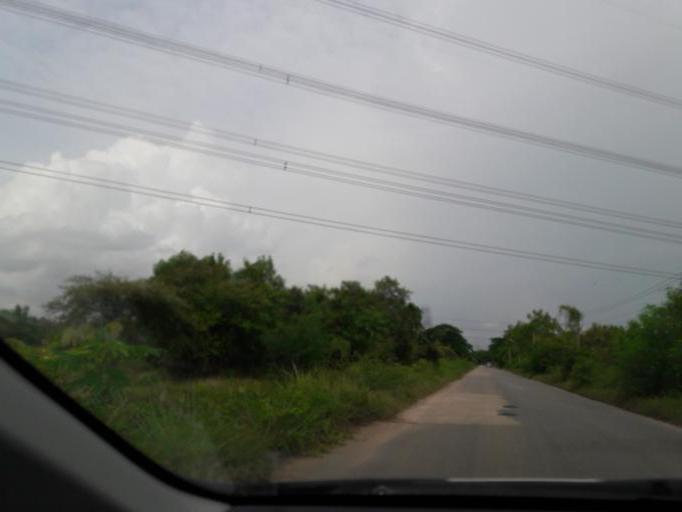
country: TH
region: Ratchaburi
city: Ratchaburi
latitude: 13.5127
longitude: 99.7841
